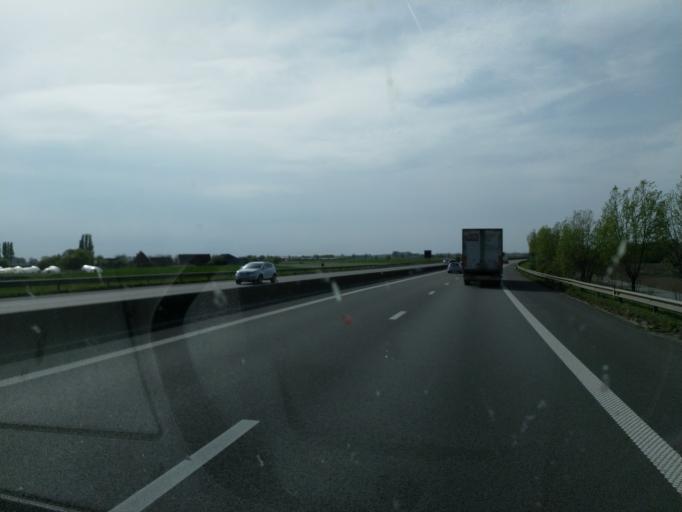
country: BE
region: Flanders
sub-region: Provincie West-Vlaanderen
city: Veurne
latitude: 51.0571
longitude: 2.6550
